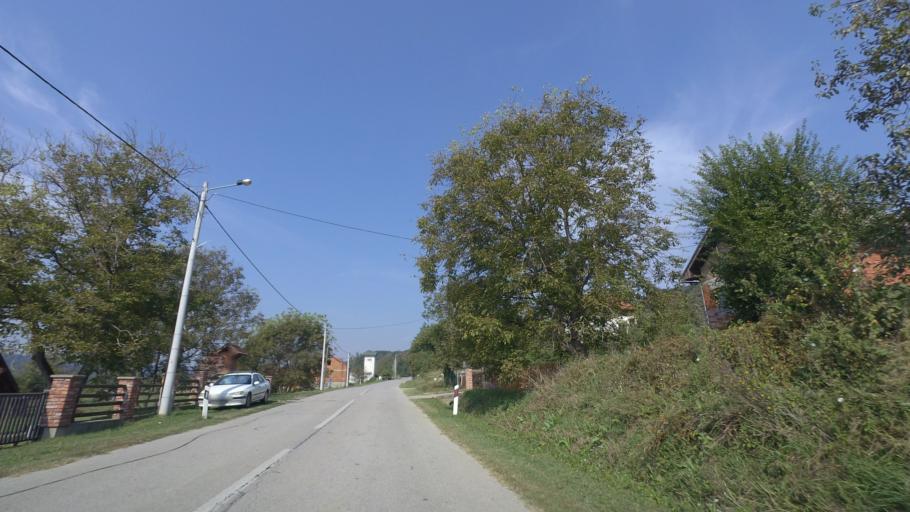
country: BA
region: Republika Srpska
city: Knezica
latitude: 45.2119
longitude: 16.6590
